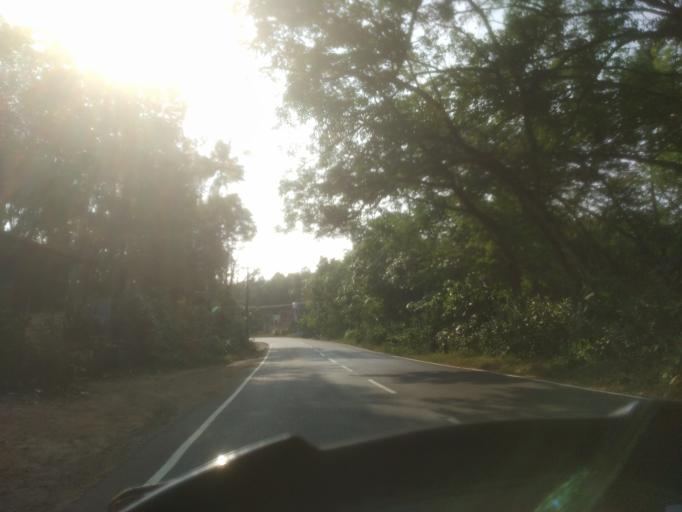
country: IN
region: Kerala
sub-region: Ernakulam
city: Piravam
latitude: 9.8327
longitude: 76.5128
